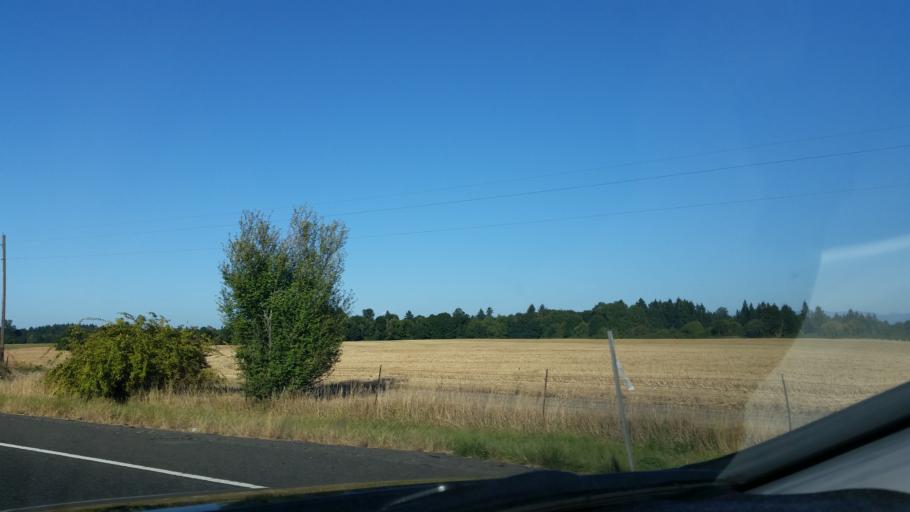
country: US
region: Oregon
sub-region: Marion County
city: Hubbard
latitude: 45.2381
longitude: -122.8039
